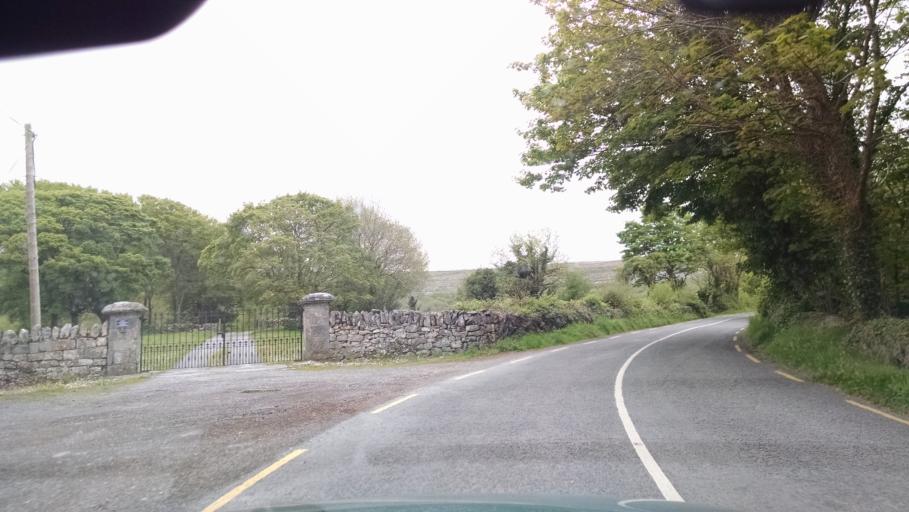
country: IE
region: Connaught
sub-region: County Galway
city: Bearna
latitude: 53.0902
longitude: -9.1581
